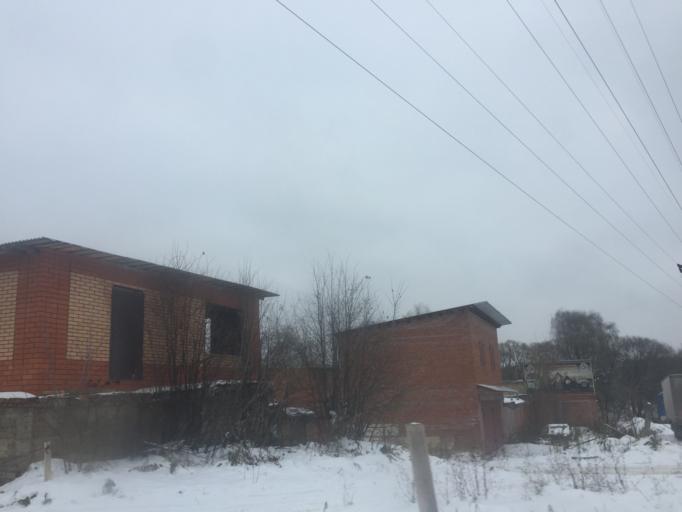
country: RU
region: Tula
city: Tula
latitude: 54.1669
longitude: 37.6218
